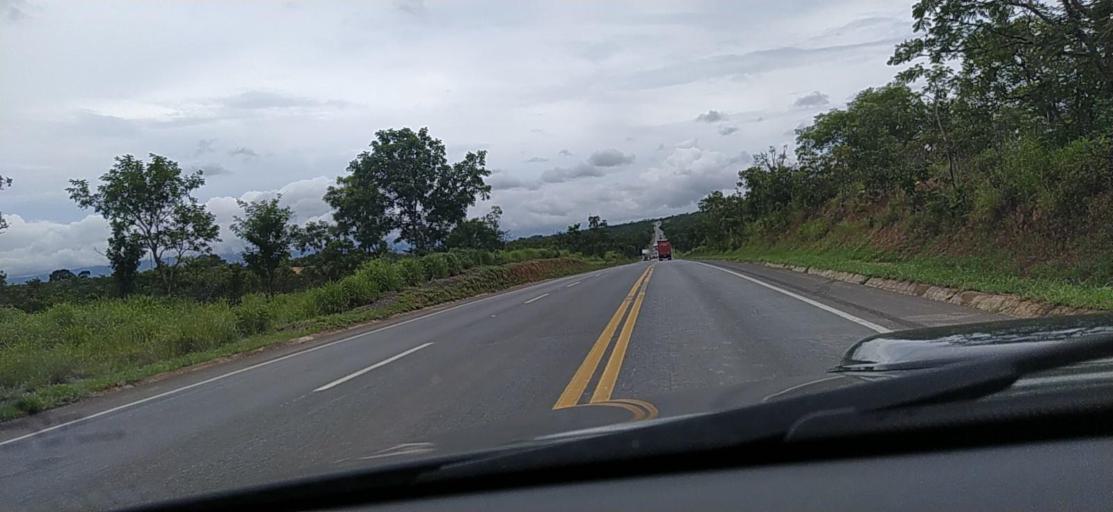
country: BR
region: Minas Gerais
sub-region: Corinto
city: Corinto
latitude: -18.3119
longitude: -44.4194
